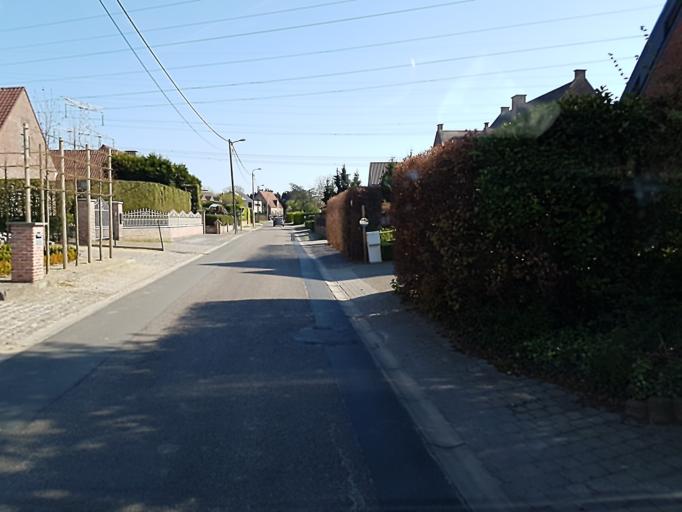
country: BE
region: Flanders
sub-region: Provincie Oost-Vlaanderen
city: Temse
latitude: 51.1408
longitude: 4.2196
